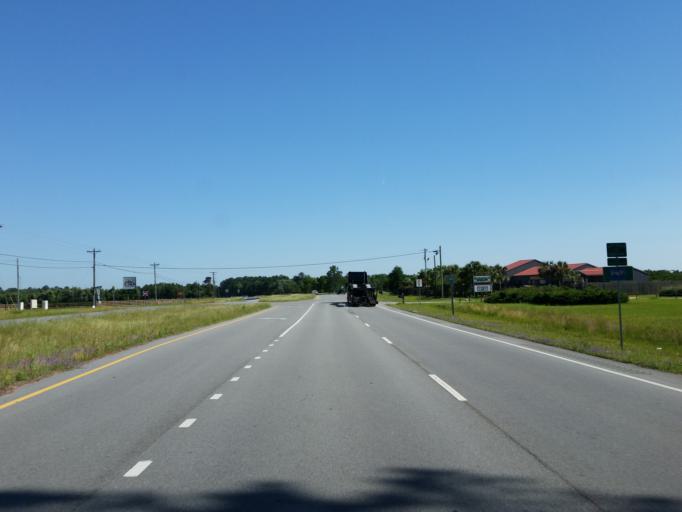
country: US
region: Georgia
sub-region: Lowndes County
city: Valdosta
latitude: 30.7756
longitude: -83.2315
